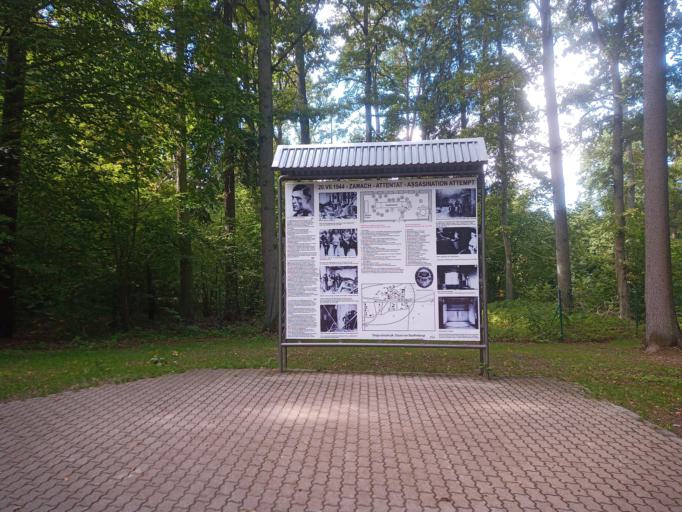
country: PL
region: Warmian-Masurian Voivodeship
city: Gierloz
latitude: 54.0810
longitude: 21.4960
